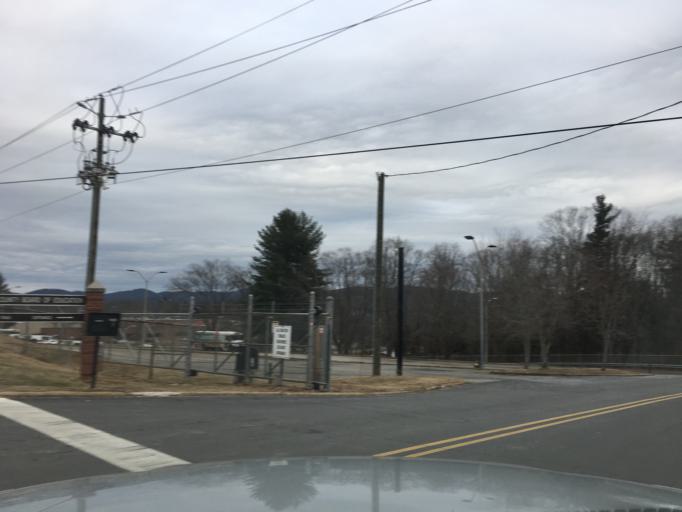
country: US
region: North Carolina
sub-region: Buncombe County
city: Woodfin
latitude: 35.6044
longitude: -82.5865
